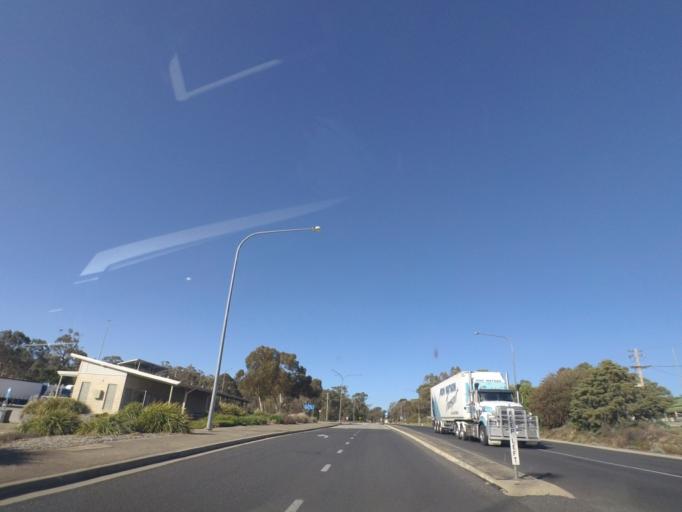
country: AU
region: New South Wales
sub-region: Wagga Wagga
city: Forest Hill
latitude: -35.2761
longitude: 147.7382
